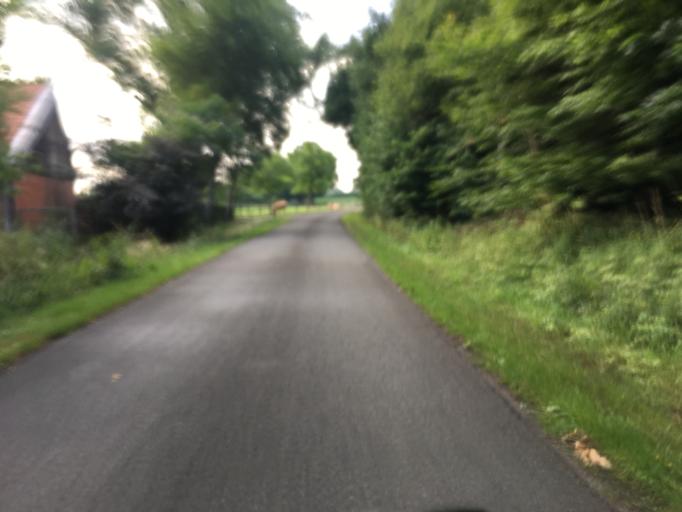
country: DE
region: North Rhine-Westphalia
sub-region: Regierungsbezirk Munster
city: Greven
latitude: 52.0530
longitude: 7.5601
